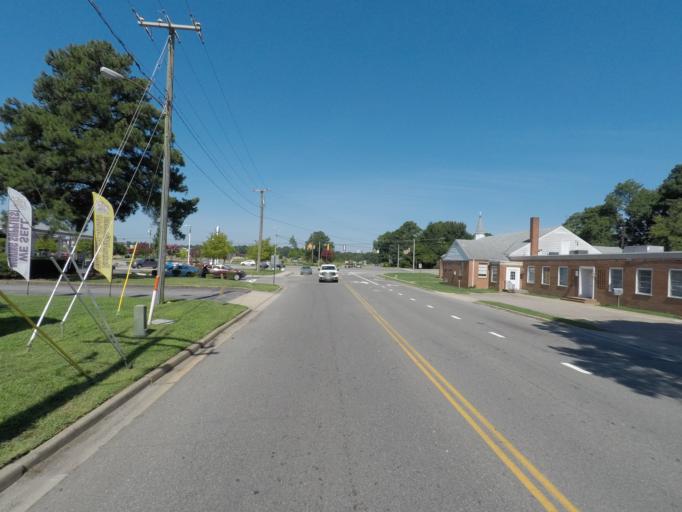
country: US
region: Virginia
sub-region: Henrico County
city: Dumbarton
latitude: 37.5924
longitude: -77.4920
